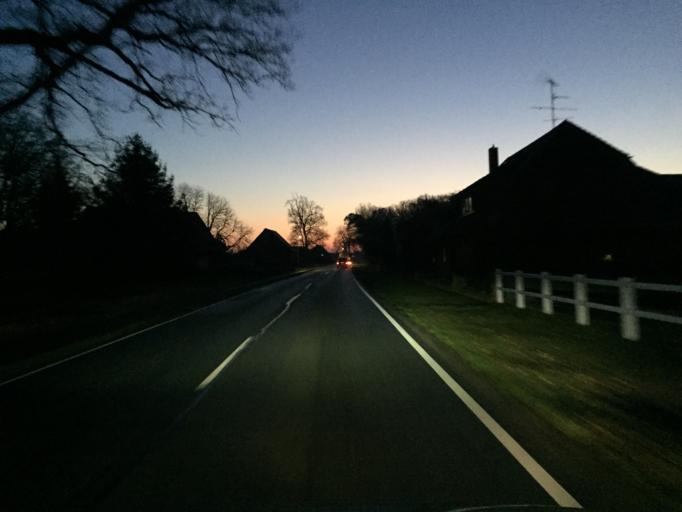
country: DE
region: Lower Saxony
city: Borstel
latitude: 52.5994
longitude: 8.9532
